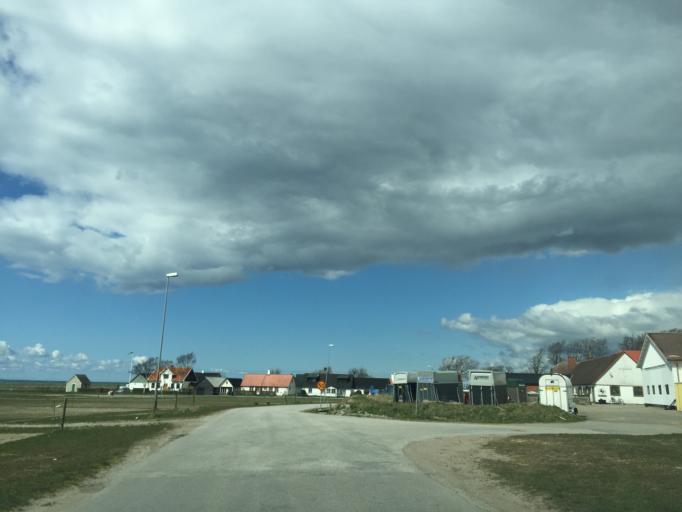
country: SE
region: Skane
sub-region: Vellinge Kommun
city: Hollviken
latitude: 55.4343
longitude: 12.9553
